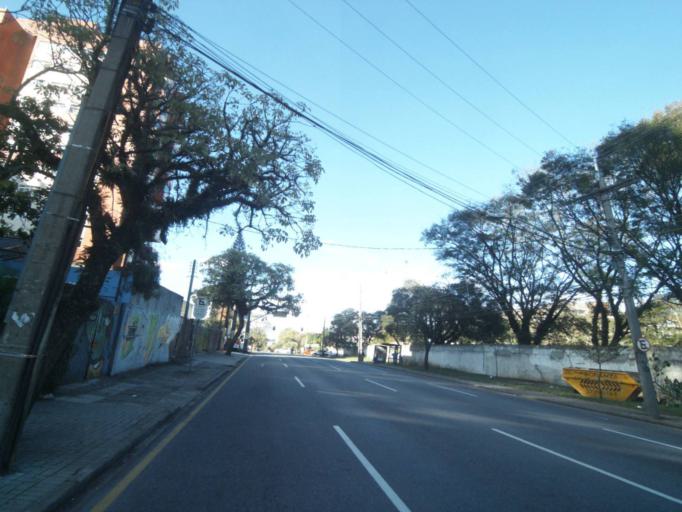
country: BR
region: Parana
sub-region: Curitiba
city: Curitiba
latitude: -25.4006
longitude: -49.2457
